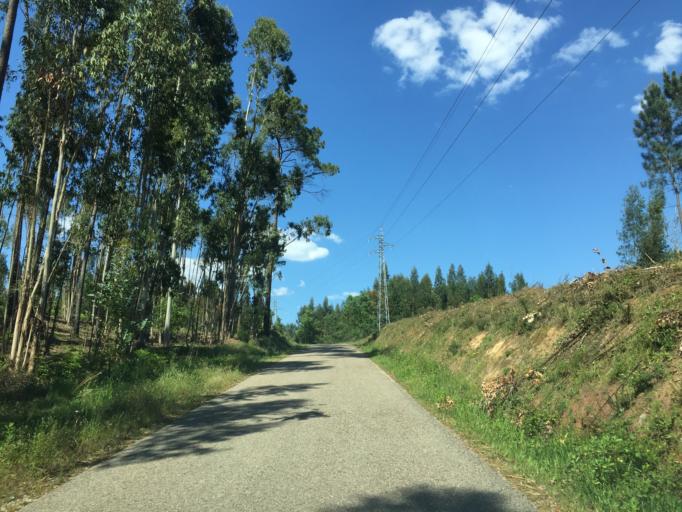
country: PT
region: Leiria
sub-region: Alvaiazere
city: Alvaiazere
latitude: 39.8472
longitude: -8.3626
